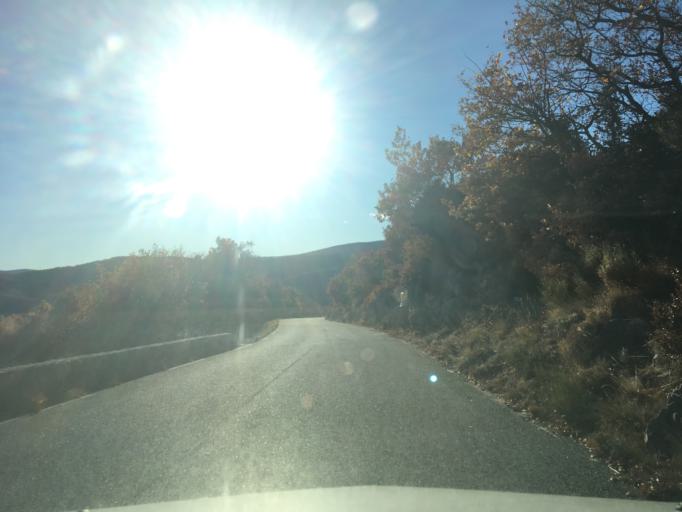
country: FR
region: Provence-Alpes-Cote d'Azur
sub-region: Departement des Alpes-de-Haute-Provence
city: Castellane
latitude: 43.7483
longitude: 6.3955
